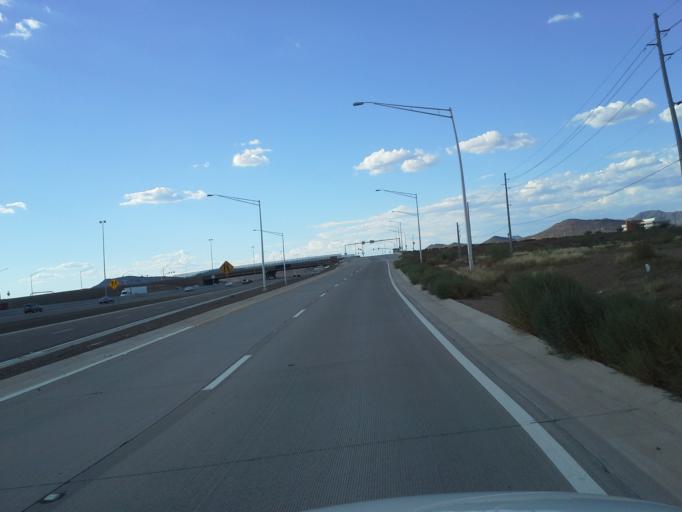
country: US
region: Arizona
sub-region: Maricopa County
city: Anthem
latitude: 33.7797
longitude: -112.1308
